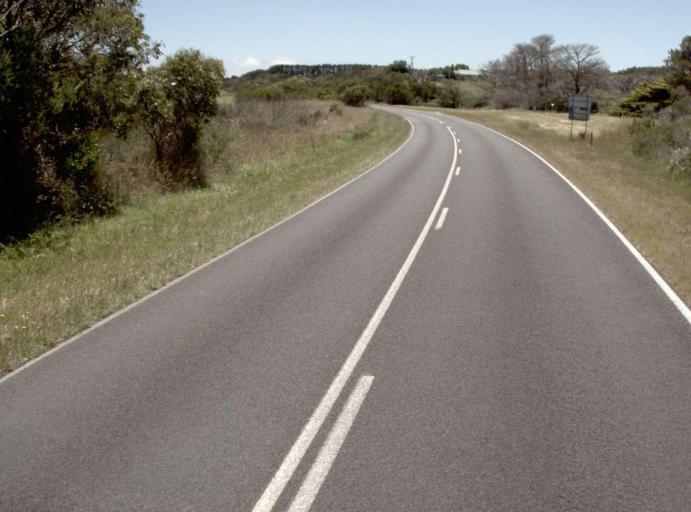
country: AU
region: Victoria
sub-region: Latrobe
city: Morwell
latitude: -38.8420
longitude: 146.2421
